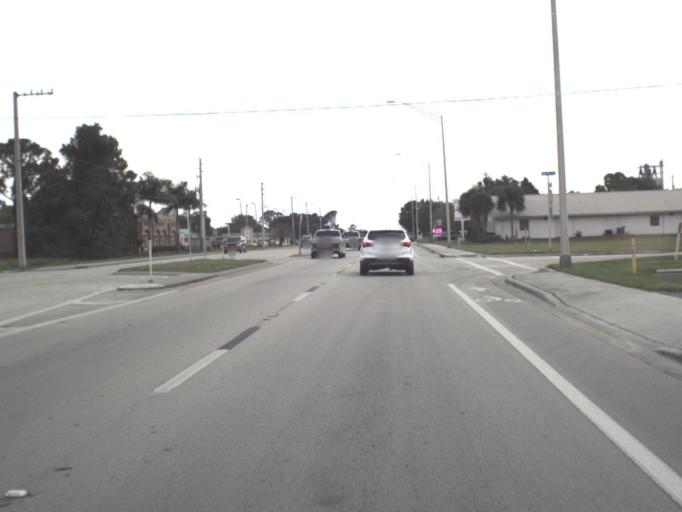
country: US
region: Florida
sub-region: Okeechobee County
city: Okeechobee
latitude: 27.2574
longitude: -80.8300
